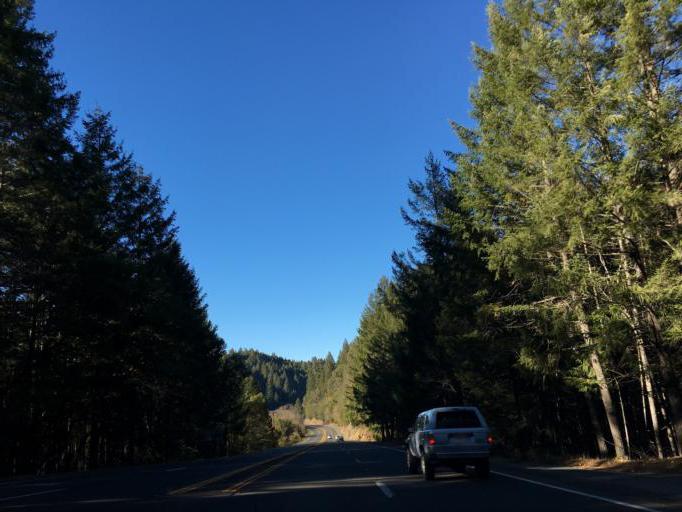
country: US
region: California
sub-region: Mendocino County
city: Brooktrails
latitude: 39.5239
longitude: -123.3985
